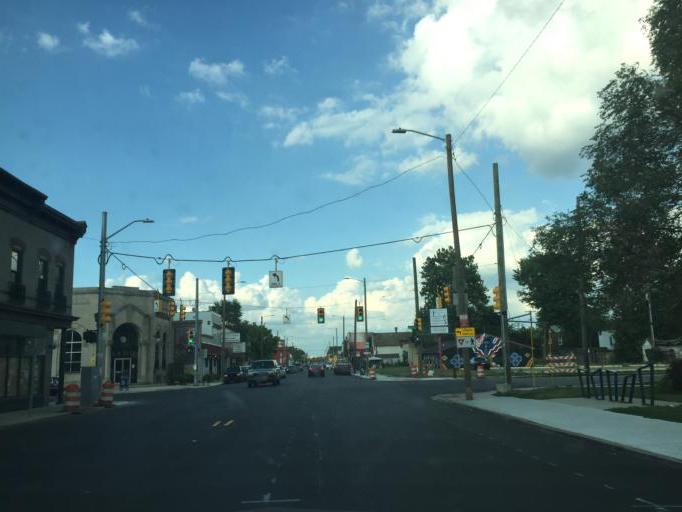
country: US
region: Michigan
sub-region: Wayne County
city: Detroit
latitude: 42.3208
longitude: -83.0944
